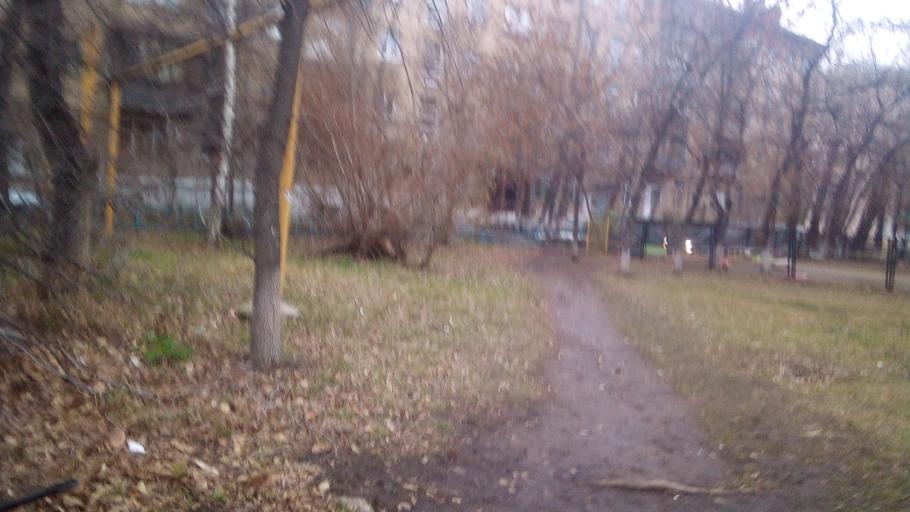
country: RU
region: Chelyabinsk
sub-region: Gorod Chelyabinsk
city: Chelyabinsk
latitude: 55.1584
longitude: 61.3826
